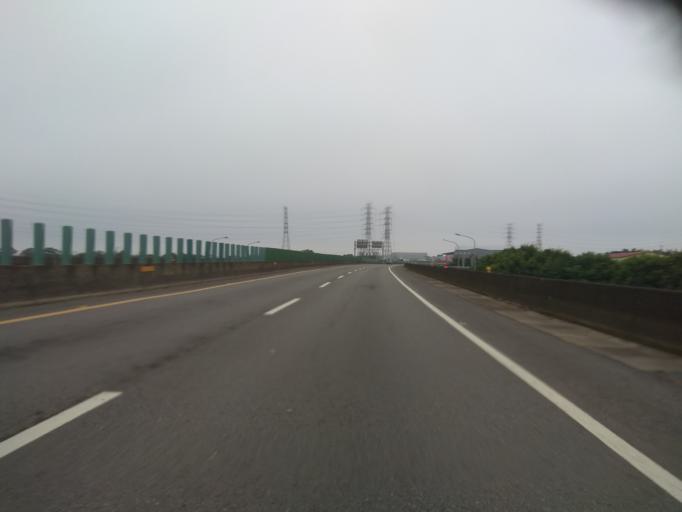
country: TW
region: Taiwan
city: Taoyuan City
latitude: 24.9847
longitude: 121.1280
